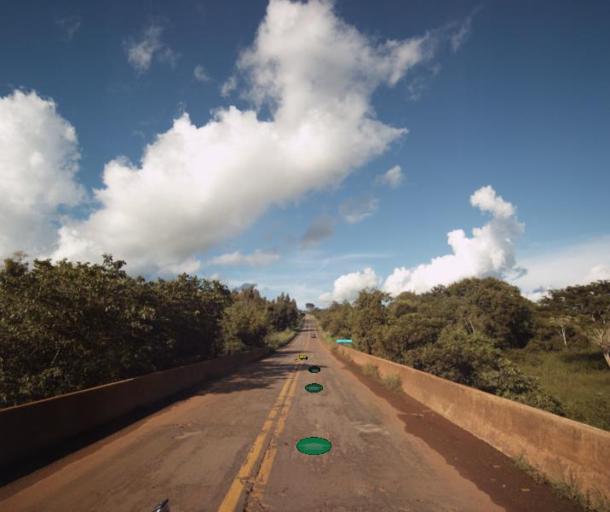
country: BR
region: Goias
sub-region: Itaberai
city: Itaberai
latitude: -15.9999
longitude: -49.7474
